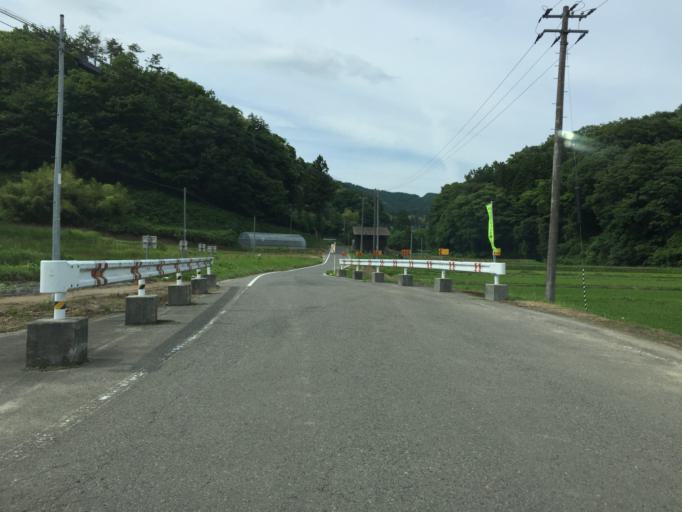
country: JP
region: Fukushima
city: Funehikimachi-funehiki
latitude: 37.4501
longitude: 140.6406
